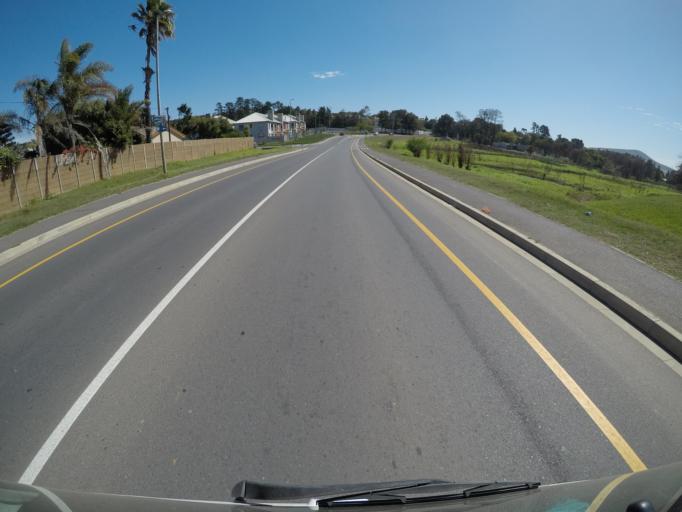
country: ZA
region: Western Cape
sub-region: City of Cape Town
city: Kraaifontein
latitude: -33.8292
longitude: 18.6387
